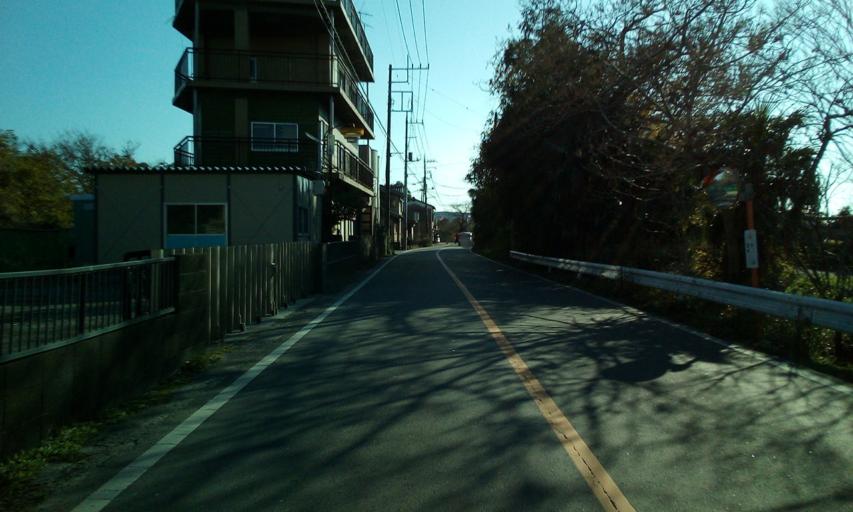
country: JP
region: Saitama
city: Kasukabe
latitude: 35.9824
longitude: 139.7970
